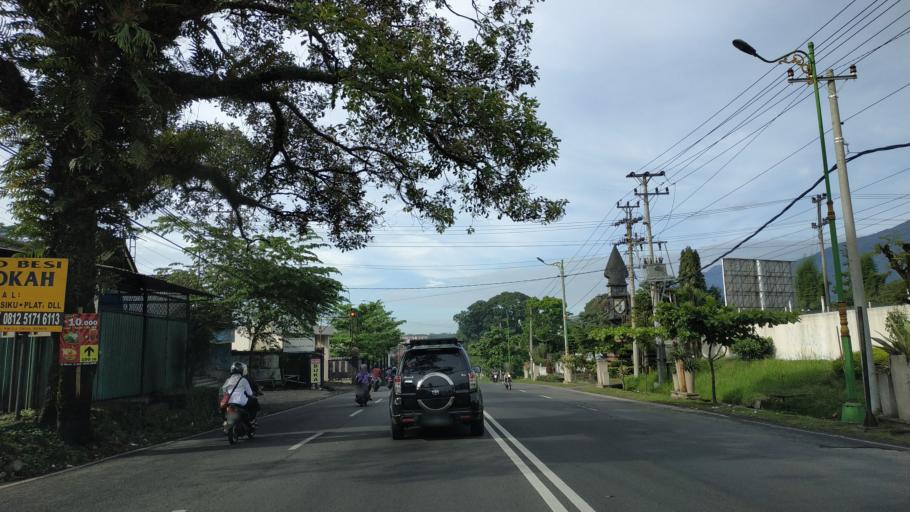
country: ID
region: Central Java
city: Salatiga
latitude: -7.3745
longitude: 110.5151
